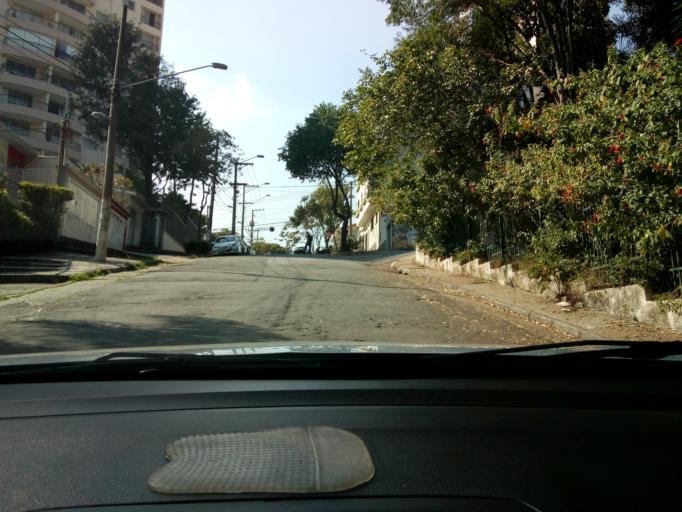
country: BR
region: Sao Paulo
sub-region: Sao Paulo
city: Sao Paulo
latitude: -23.5730
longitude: -46.6265
